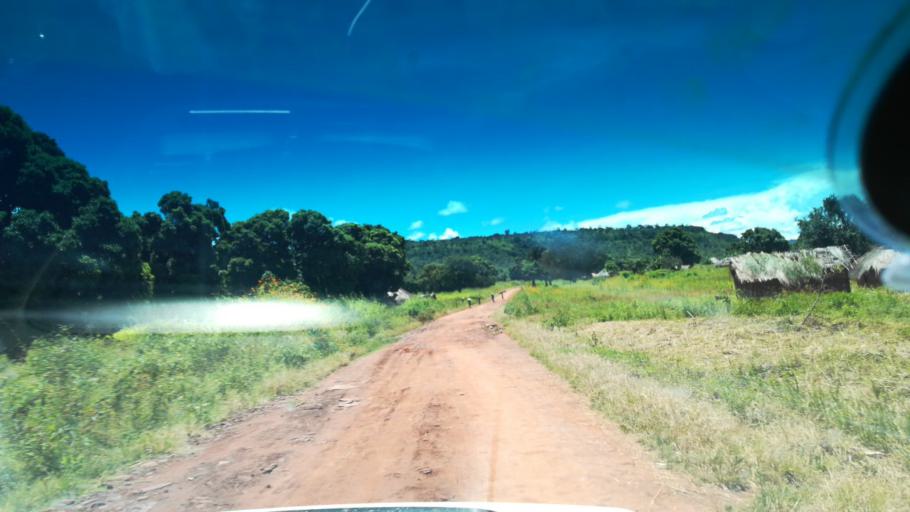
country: ZM
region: Luapula
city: Nchelenge
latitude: -8.7734
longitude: 28.6439
